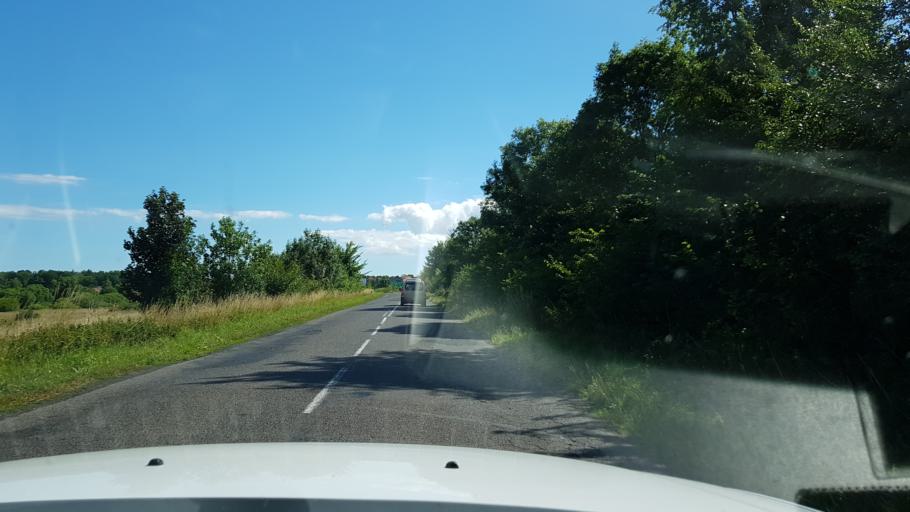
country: PL
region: West Pomeranian Voivodeship
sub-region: Powiat gryficki
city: Trzebiatow
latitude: 54.0501
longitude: 15.2470
